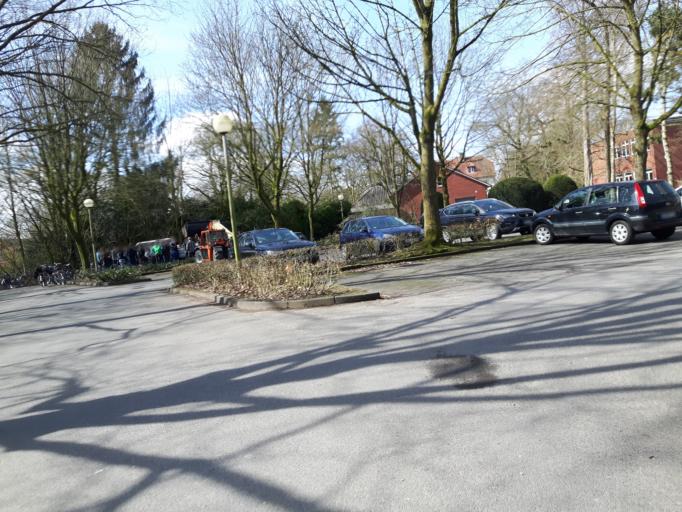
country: DE
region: North Rhine-Westphalia
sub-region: Regierungsbezirk Munster
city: Senden
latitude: 51.8544
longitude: 7.4869
